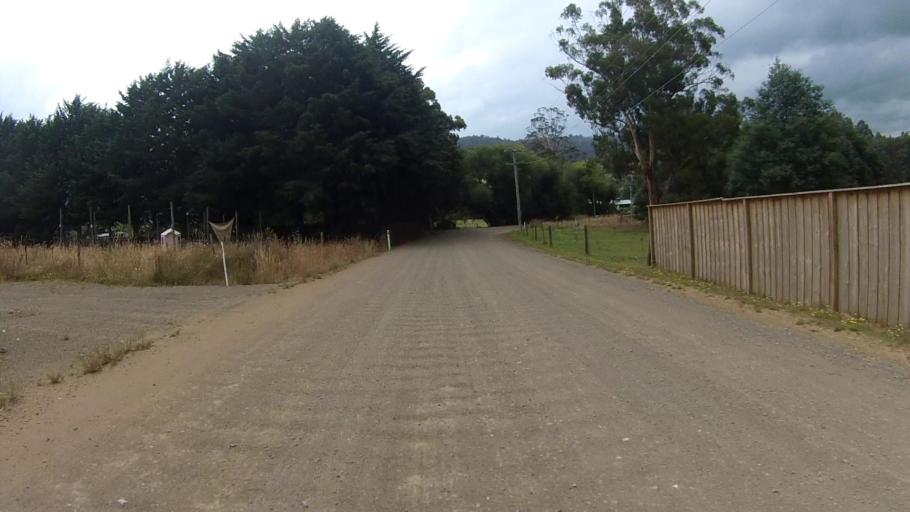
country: AU
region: Tasmania
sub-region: Huon Valley
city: Huonville
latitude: -42.9812
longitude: 147.0548
